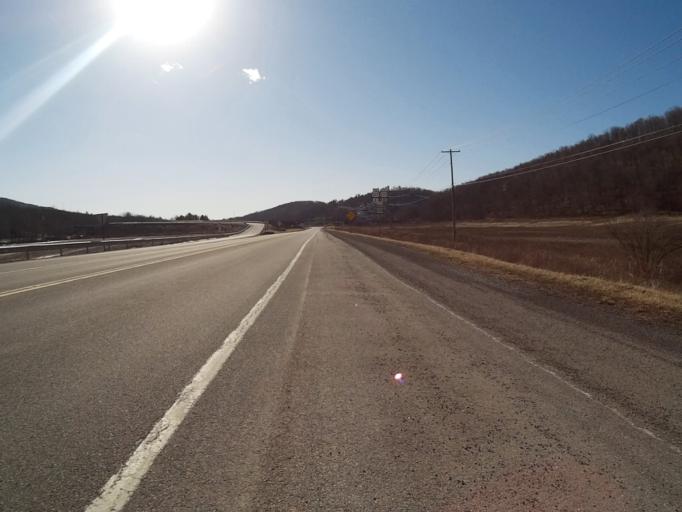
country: US
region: Pennsylvania
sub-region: Centre County
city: Stormstown
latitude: 40.8315
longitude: -78.0119
